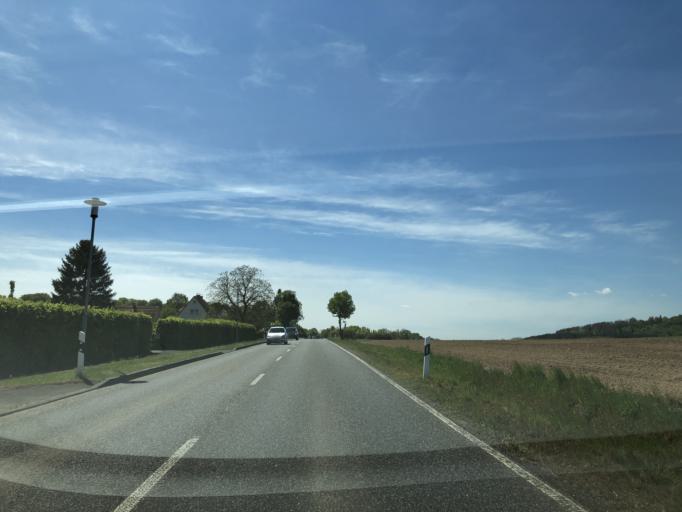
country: DE
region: Hesse
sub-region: Regierungsbezirk Kassel
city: Homberg
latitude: 51.0625
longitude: 9.4450
